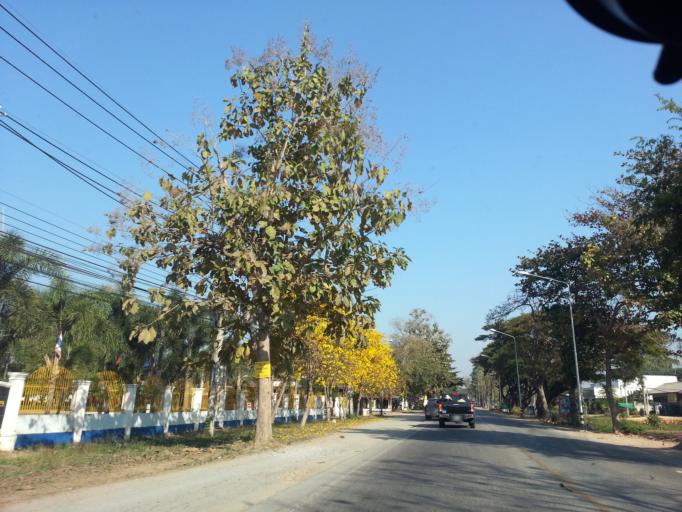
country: TH
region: Chiang Mai
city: San Sai
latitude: 18.9742
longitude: 98.9824
